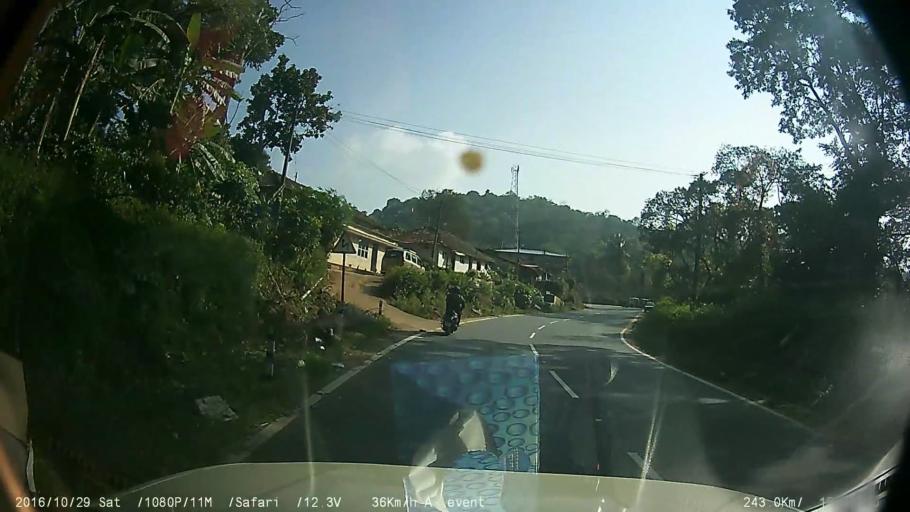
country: IN
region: Karnataka
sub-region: Kodagu
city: Madikeri
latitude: 12.4341
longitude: 75.7860
